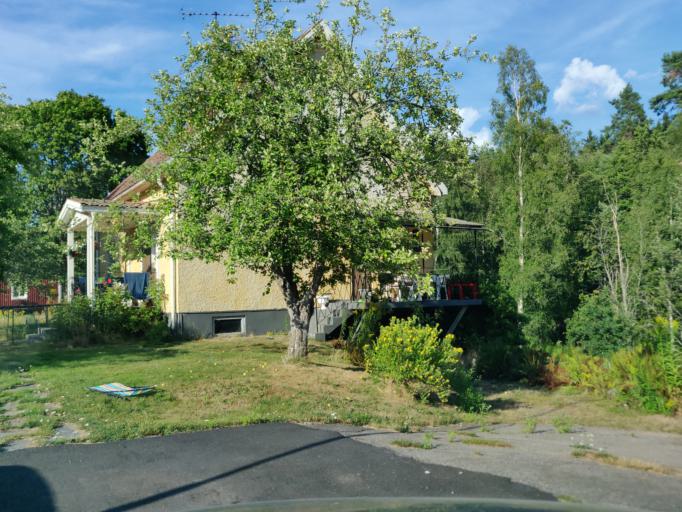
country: SE
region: Vaermland
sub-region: Hagfors Kommun
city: Hagfors
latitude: 60.0309
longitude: 13.7073
